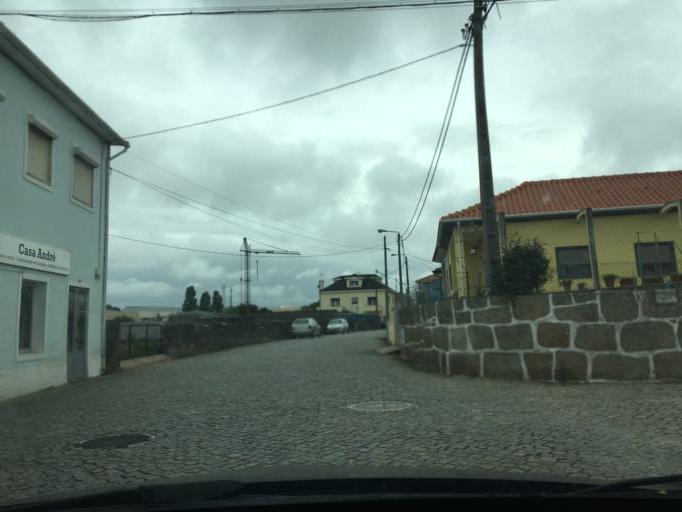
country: PT
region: Porto
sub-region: Matosinhos
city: Santa Cruz do Bispo
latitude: 41.2305
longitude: -8.6604
